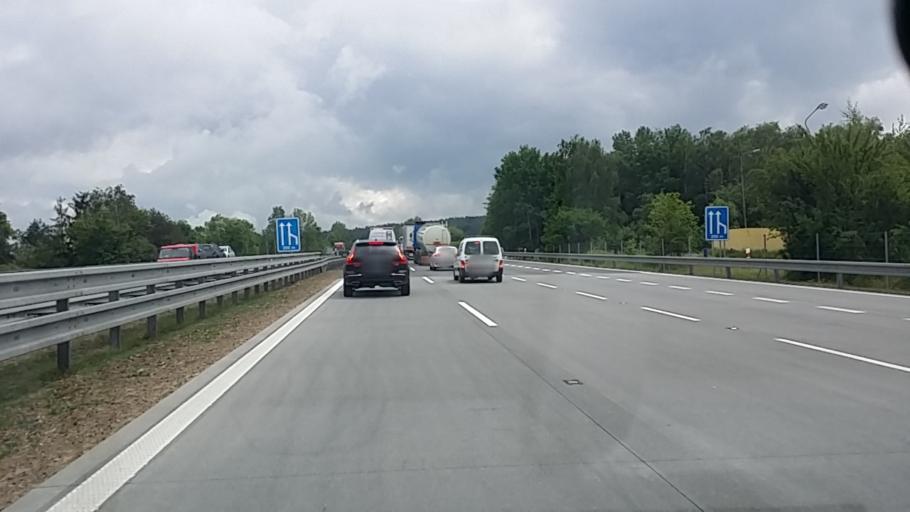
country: CZ
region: Central Bohemia
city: Trhovy Stepanov
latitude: 49.7250
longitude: 15.0479
